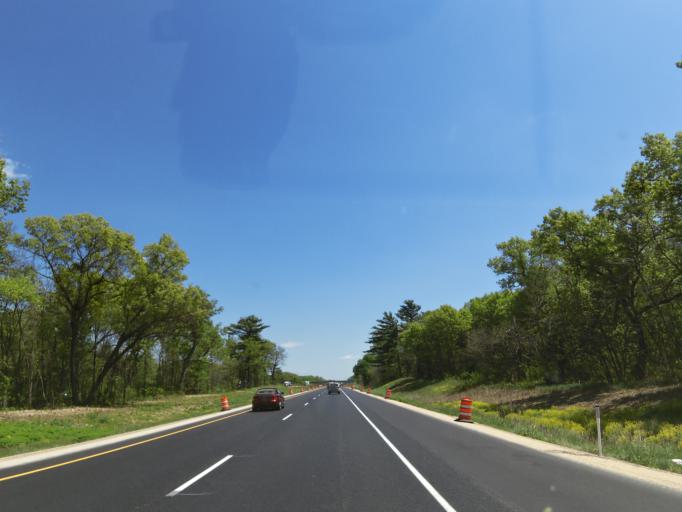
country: US
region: Wisconsin
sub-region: Juneau County
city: Mauston
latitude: 43.7688
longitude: -89.9968
